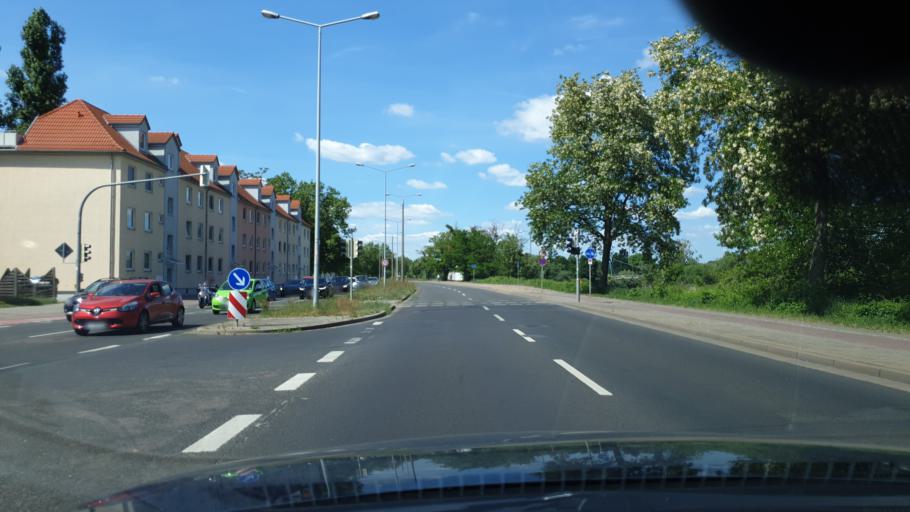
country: DE
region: Saxony-Anhalt
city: Dessau
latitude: 51.8171
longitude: 12.2501
